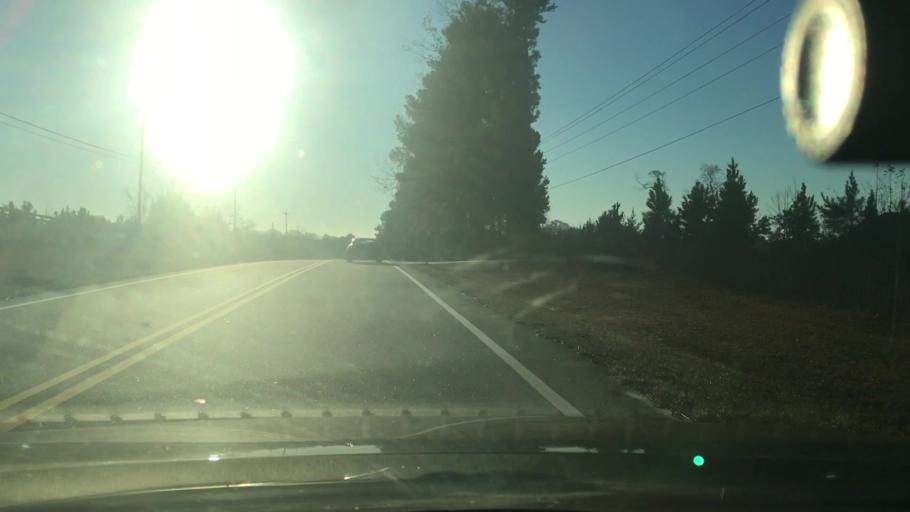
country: US
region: Georgia
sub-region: Coweta County
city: Senoia
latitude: 33.2738
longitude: -84.5306
